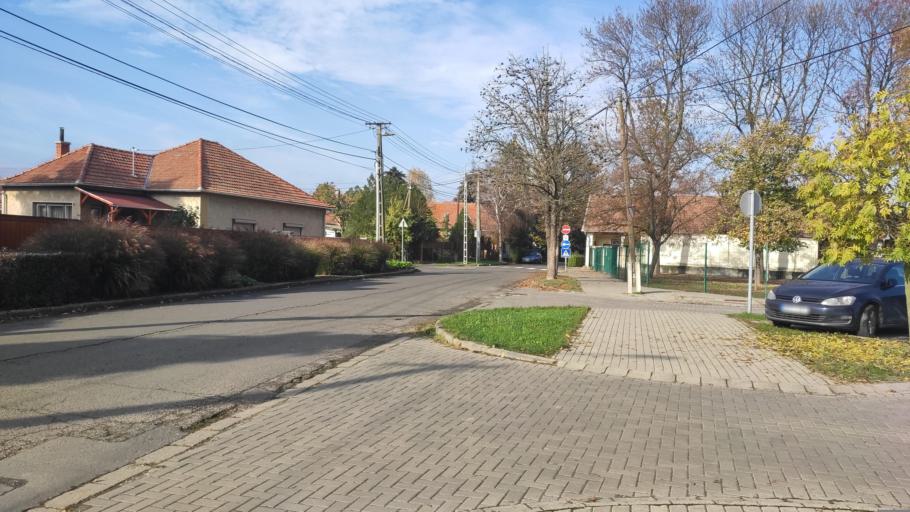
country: HU
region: Bekes
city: Bekes
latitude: 46.7659
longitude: 21.1314
